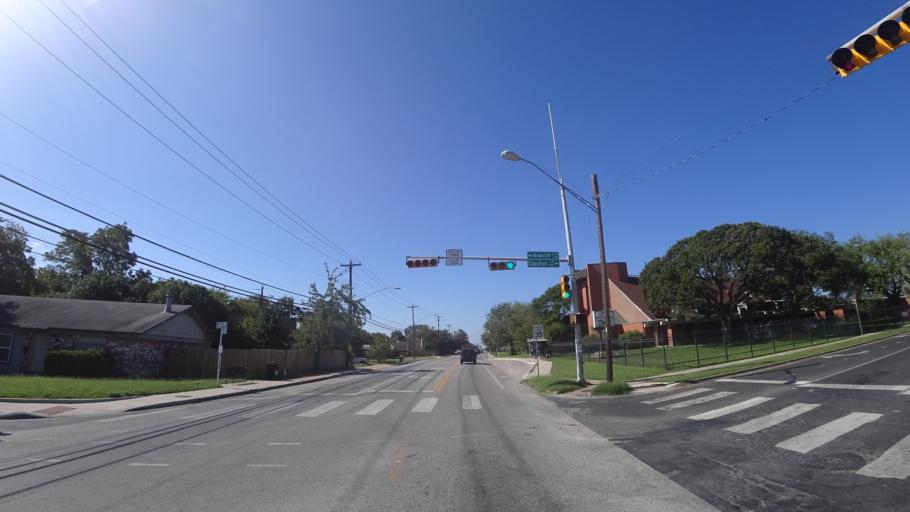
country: US
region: Texas
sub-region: Travis County
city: Austin
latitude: 30.3173
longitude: -97.6997
